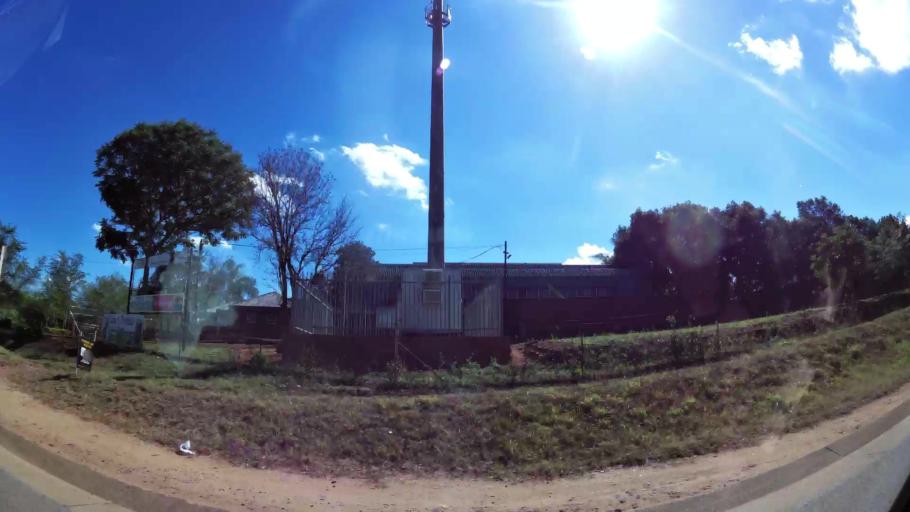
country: ZA
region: Limpopo
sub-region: Mopani District Municipality
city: Tzaneen
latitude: -23.8204
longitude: 30.1643
